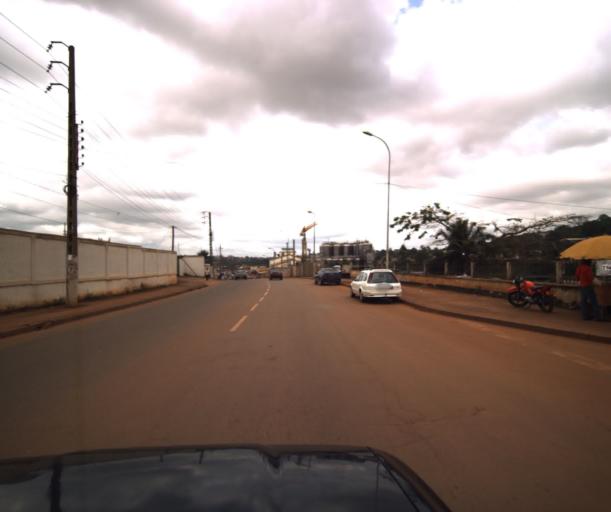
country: CM
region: Centre
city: Yaounde
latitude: 3.8427
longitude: 11.5154
